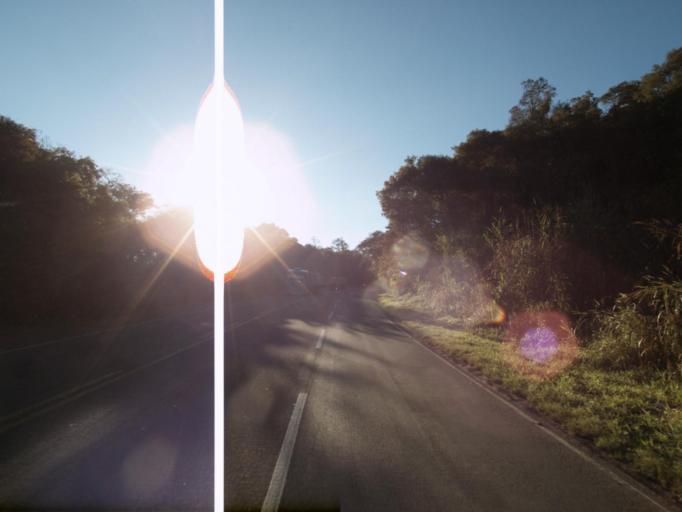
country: BR
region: Santa Catarina
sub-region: Chapeco
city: Chapeco
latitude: -26.9167
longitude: -52.8641
